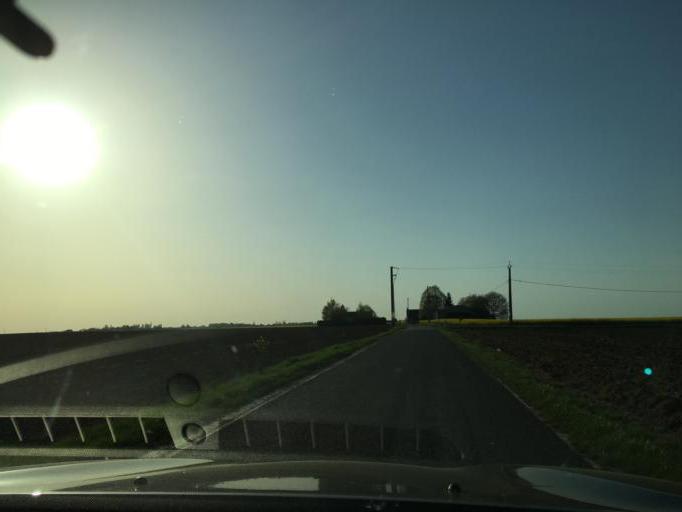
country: FR
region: Centre
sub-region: Departement du Loir-et-Cher
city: Ouzouer-le-Marche
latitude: 47.9038
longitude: 1.5619
